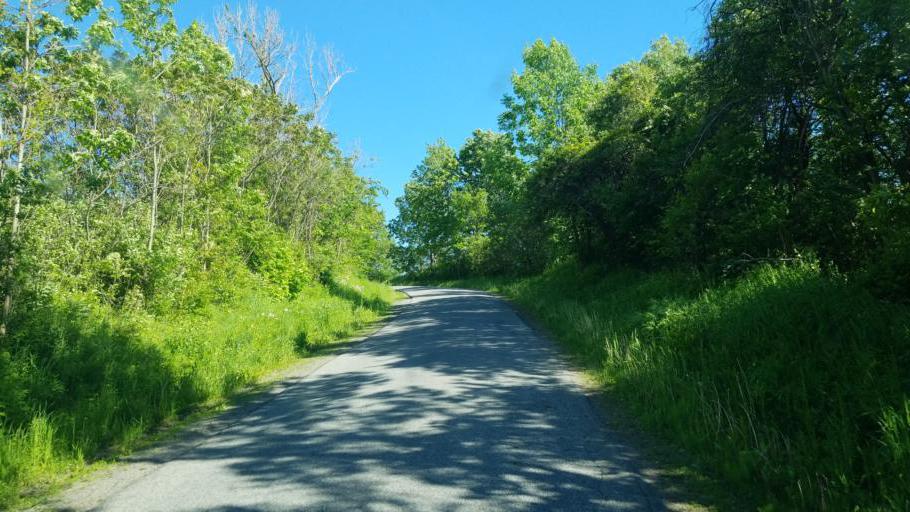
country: US
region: New York
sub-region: Montgomery County
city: Saint Johnsville
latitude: 42.9865
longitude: -74.7772
